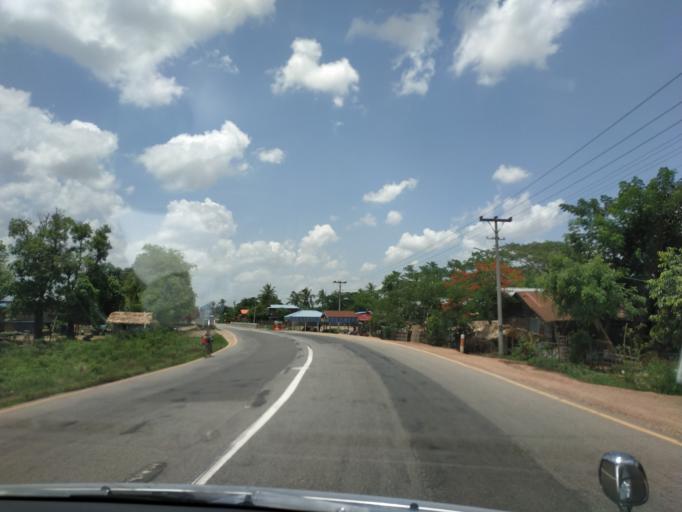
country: MM
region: Bago
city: Thanatpin
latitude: 17.5072
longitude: 96.7130
